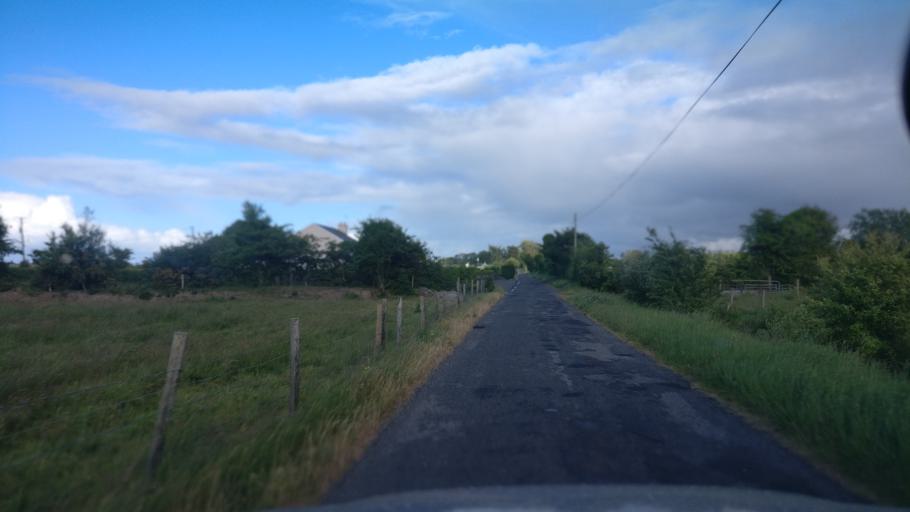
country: IE
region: Connaught
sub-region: County Galway
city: Ballinasloe
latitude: 53.2467
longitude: -8.2176
